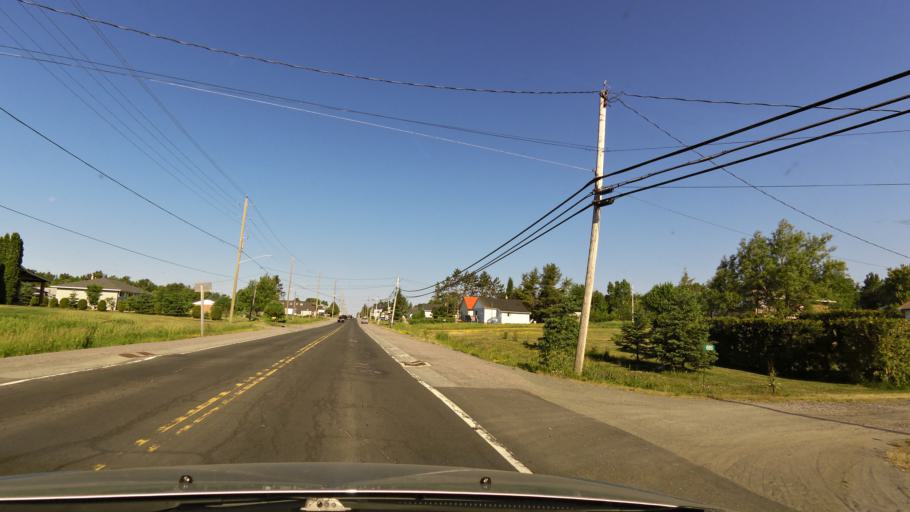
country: CA
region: Ontario
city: Greater Sudbury
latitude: 46.1047
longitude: -80.6206
